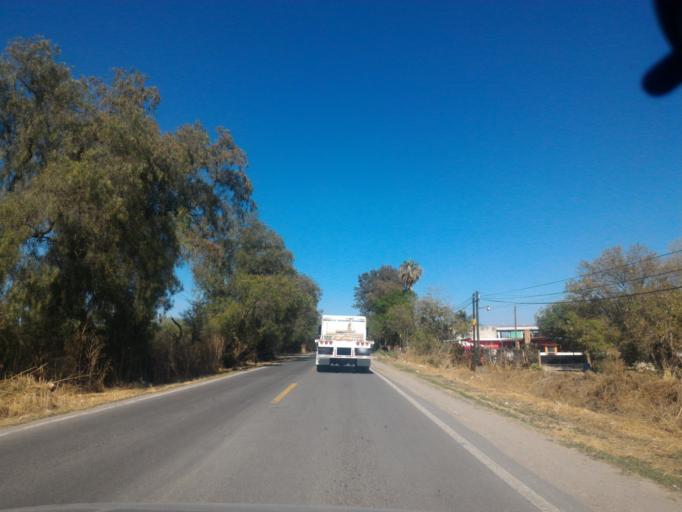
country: MX
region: Guanajuato
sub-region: Leon
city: Malagana (San Antonio del Monte)
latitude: 21.0440
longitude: -101.7621
